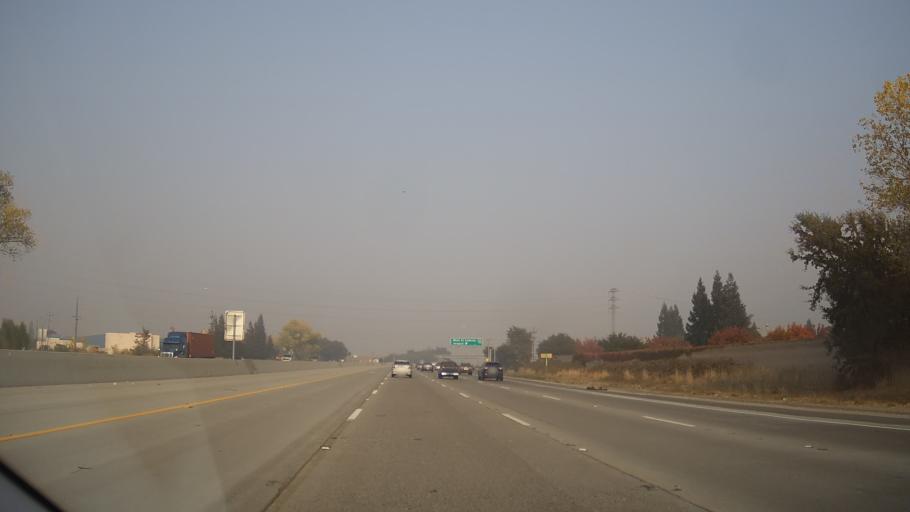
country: US
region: California
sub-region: Yolo County
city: West Sacramento
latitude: 38.6109
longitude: -121.5393
